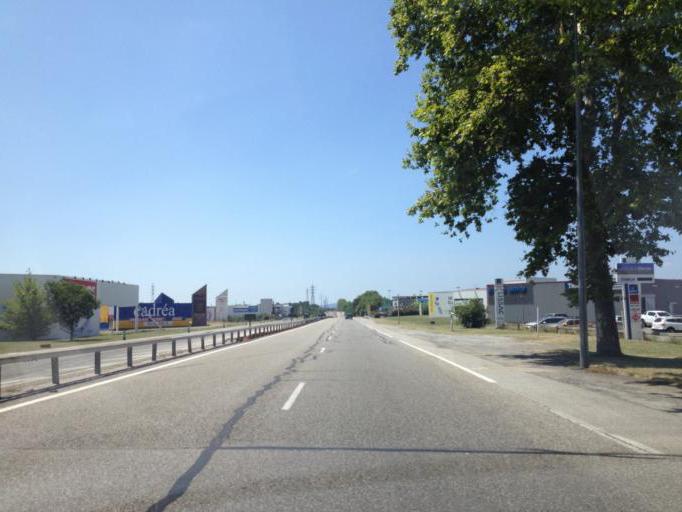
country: FR
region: Rhone-Alpes
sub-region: Departement de la Drome
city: Bourg-les-Valence
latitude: 44.9521
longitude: 4.9298
